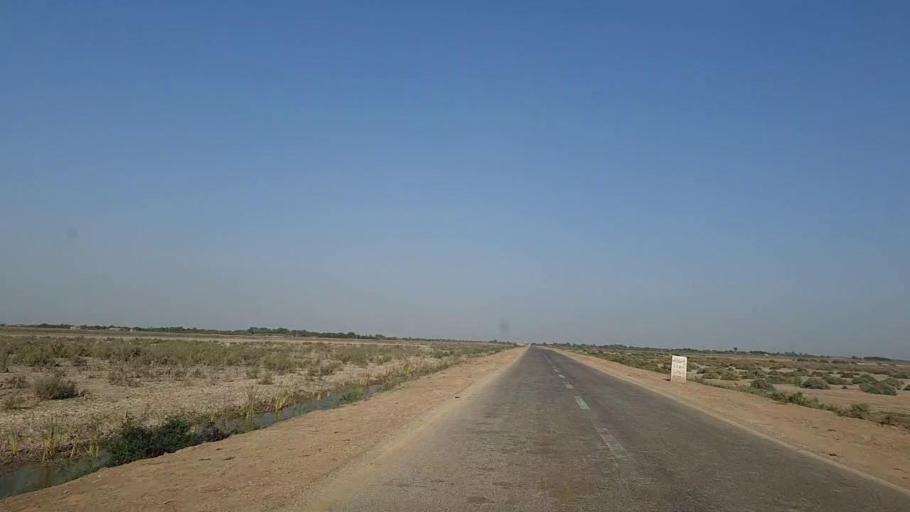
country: PK
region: Sindh
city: Jati
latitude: 24.4440
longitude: 68.3246
